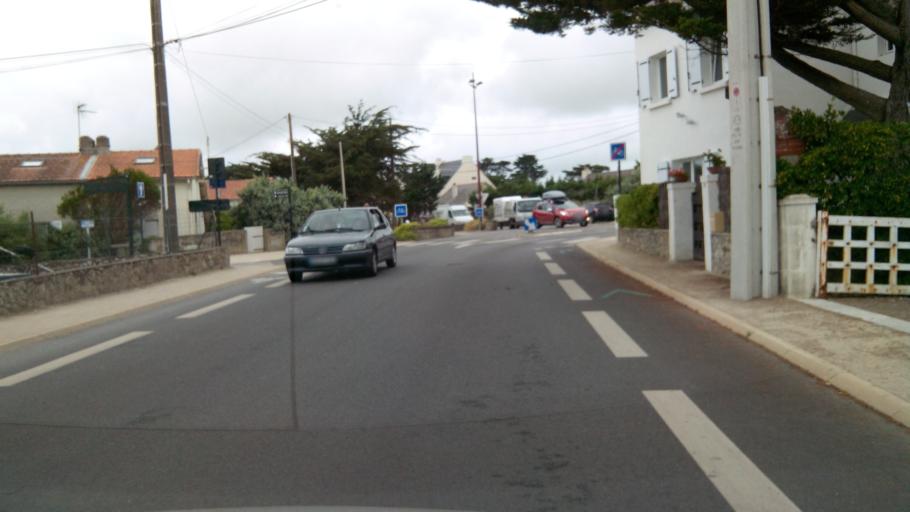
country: FR
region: Pays de la Loire
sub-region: Departement de la Loire-Atlantique
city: Batz-sur-Mer
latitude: 47.2807
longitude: -2.4957
